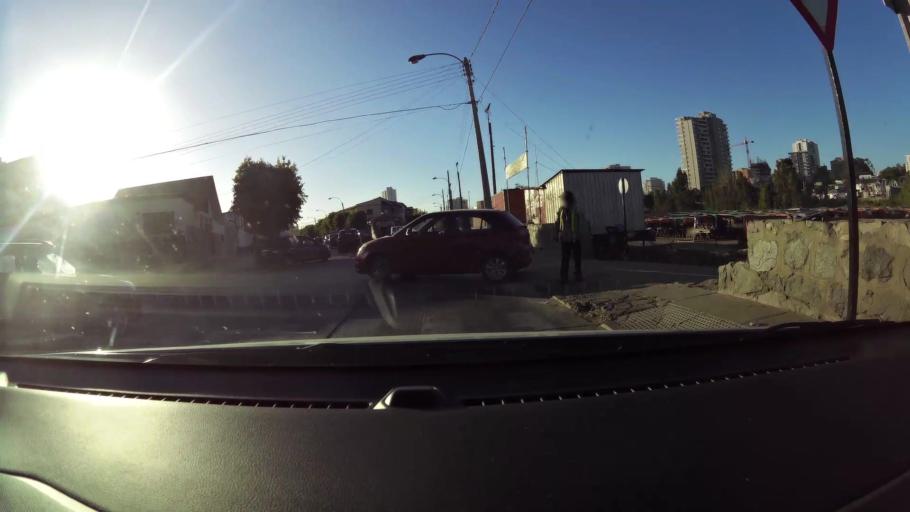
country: CL
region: Valparaiso
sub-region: Provincia de Valparaiso
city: Vina del Mar
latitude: -33.0255
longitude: -71.5420
